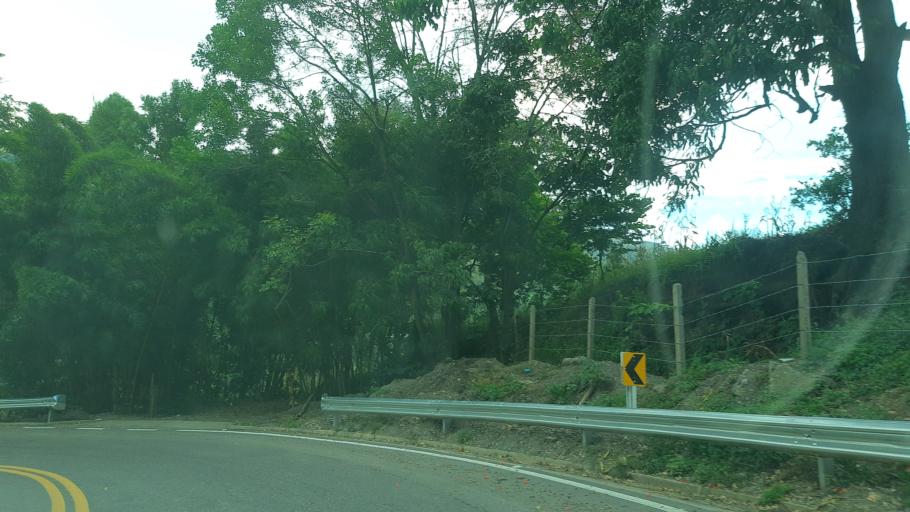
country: CO
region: Boyaca
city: Somondoco
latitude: 5.0097
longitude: -73.4321
